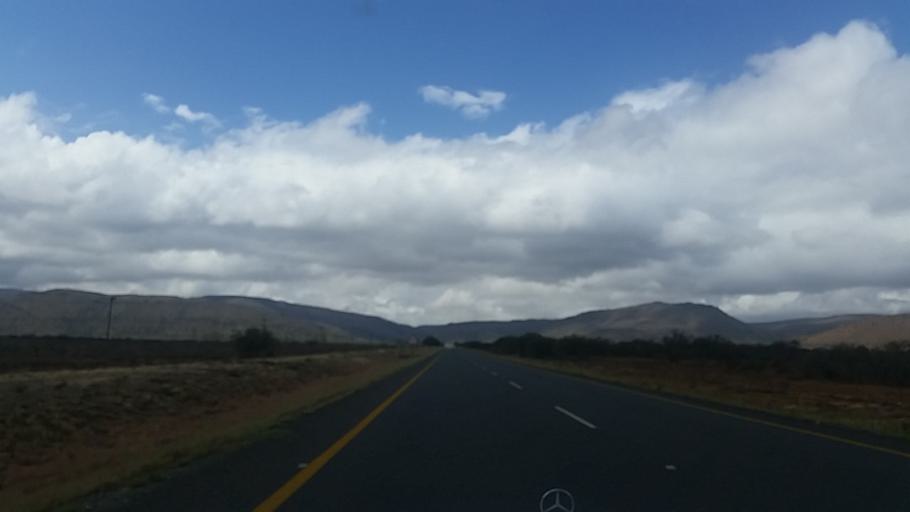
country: ZA
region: Eastern Cape
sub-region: Cacadu District Municipality
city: Graaff-Reinet
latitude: -31.9930
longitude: 24.6798
